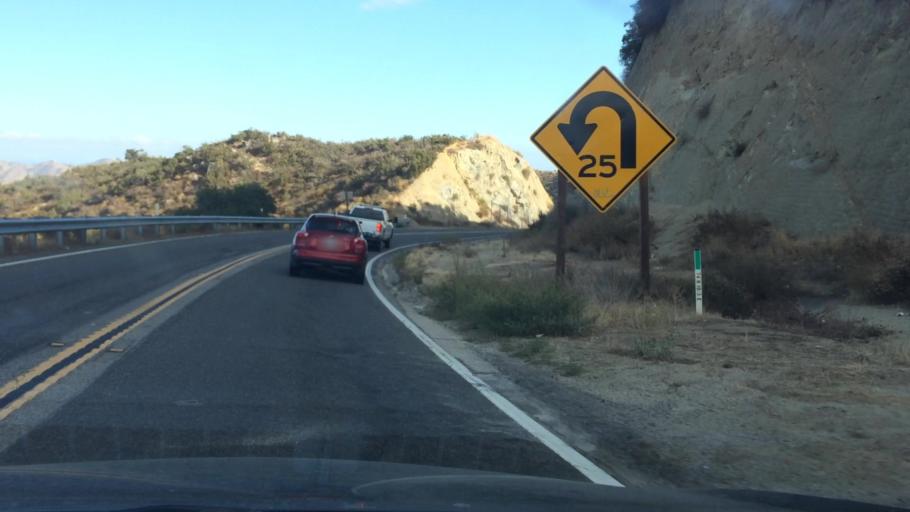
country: US
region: California
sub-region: Riverside County
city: Lakeland Village
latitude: 33.6465
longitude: -117.3719
